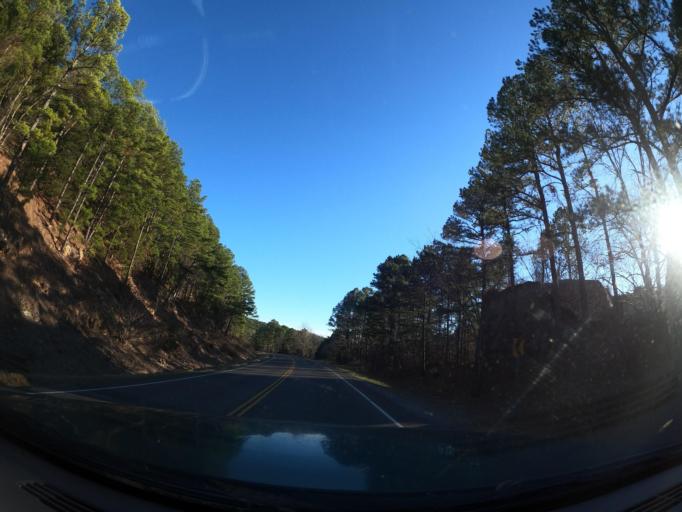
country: US
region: Oklahoma
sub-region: Latimer County
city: Wilburton
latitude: 34.9762
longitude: -95.3590
